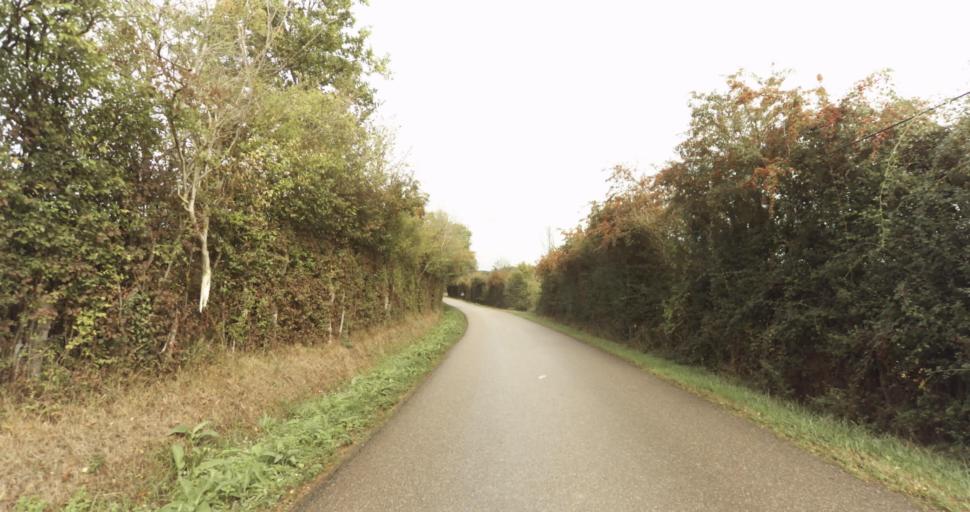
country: FR
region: Lower Normandy
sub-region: Departement de l'Orne
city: Vimoutiers
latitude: 48.8528
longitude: 0.2129
